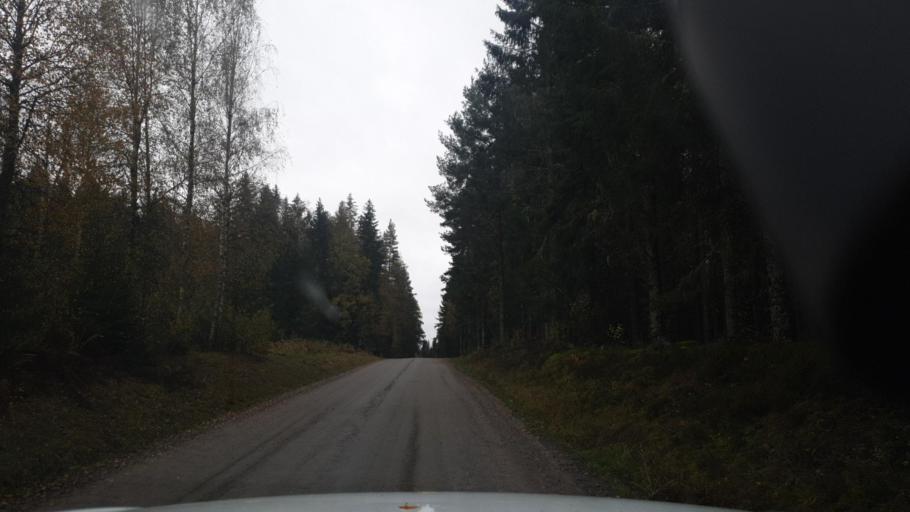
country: SE
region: Vaermland
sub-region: Karlstads Kommun
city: Edsvalla
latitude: 59.4978
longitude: 13.0290
